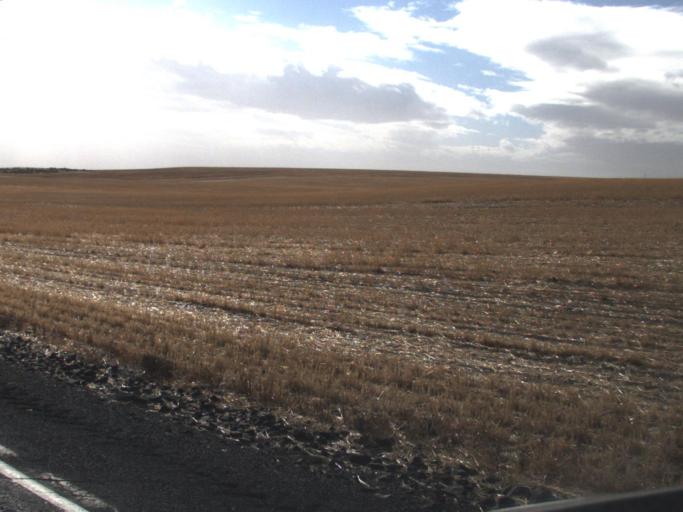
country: US
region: Washington
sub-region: Okanogan County
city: Coulee Dam
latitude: 47.5716
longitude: -118.7859
